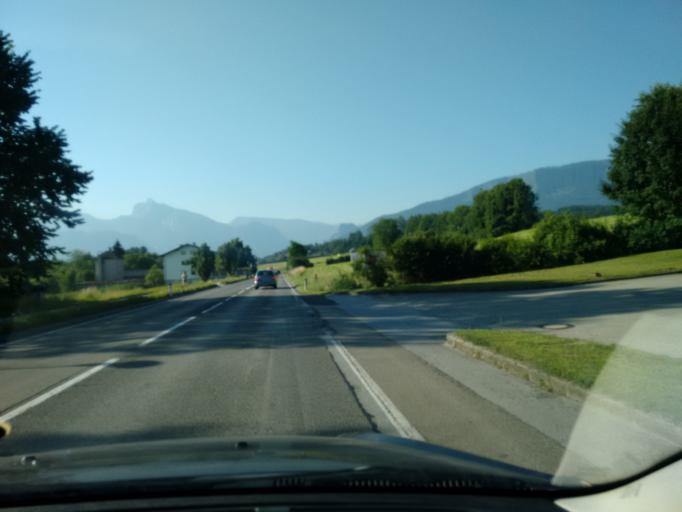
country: AT
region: Upper Austria
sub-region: Politischer Bezirk Gmunden
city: Altmunster
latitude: 47.8841
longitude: 13.7718
